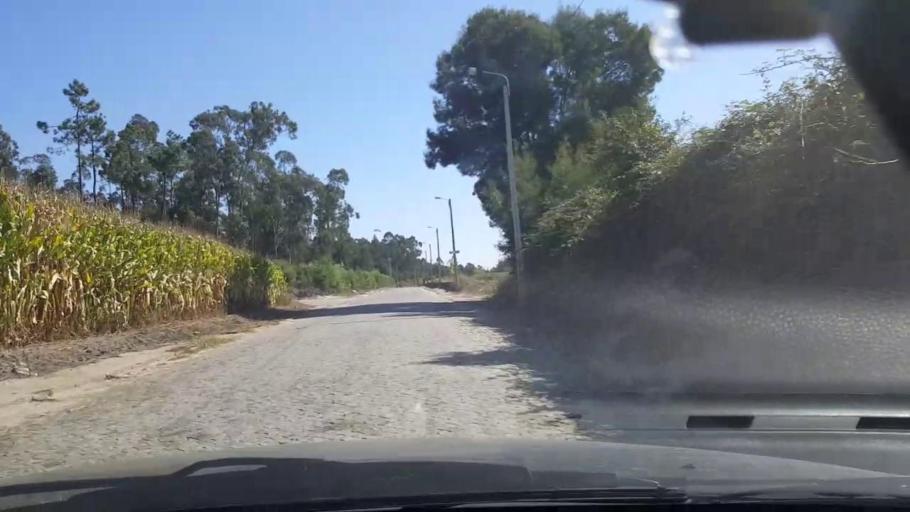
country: PT
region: Porto
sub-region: Vila do Conde
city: Arvore
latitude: 41.3165
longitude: -8.6896
